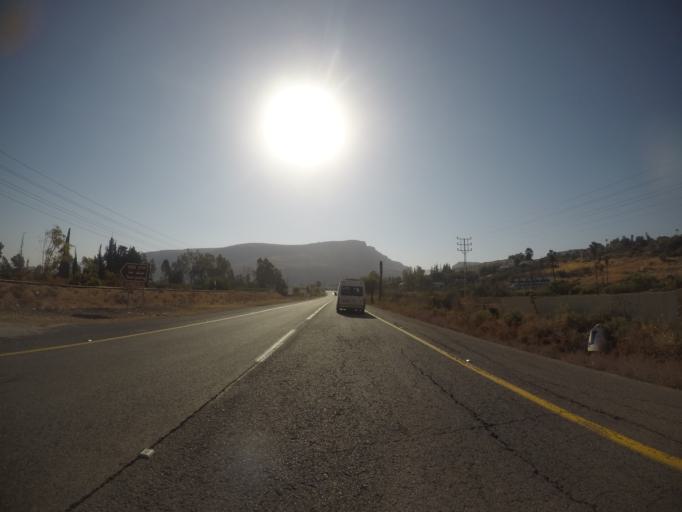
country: IL
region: Northern District
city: Tiberias
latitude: 32.8407
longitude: 35.5131
